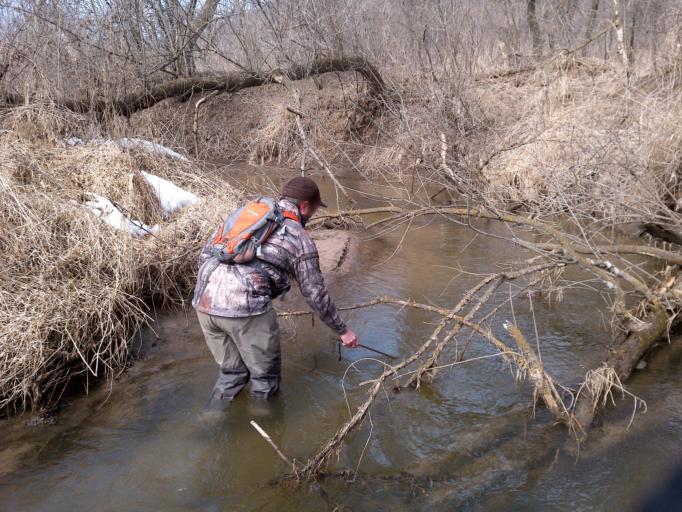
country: US
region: Minnesota
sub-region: Wabasha County
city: Lake City
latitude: 44.4384
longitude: -92.3355
